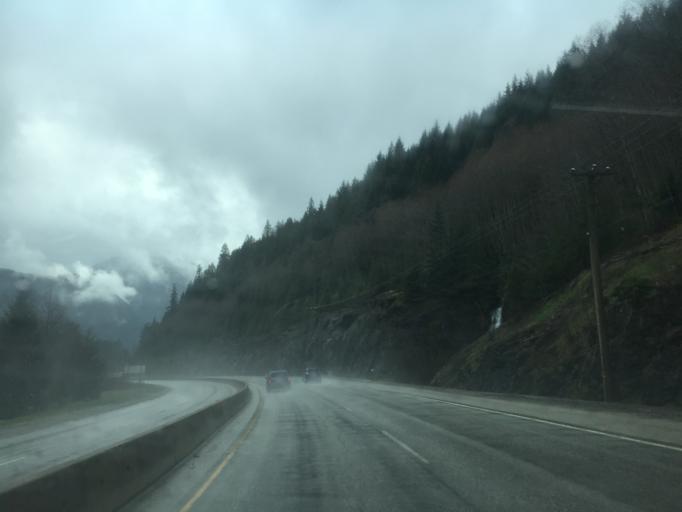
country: CA
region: British Columbia
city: Hope
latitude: 49.4898
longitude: -121.2485
